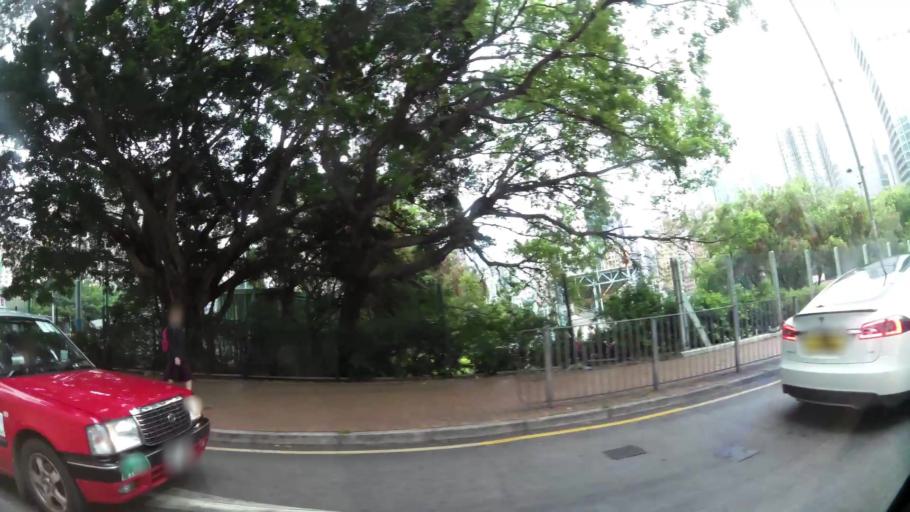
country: HK
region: Tsuen Wan
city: Tsuen Wan
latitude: 22.3581
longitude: 114.1241
